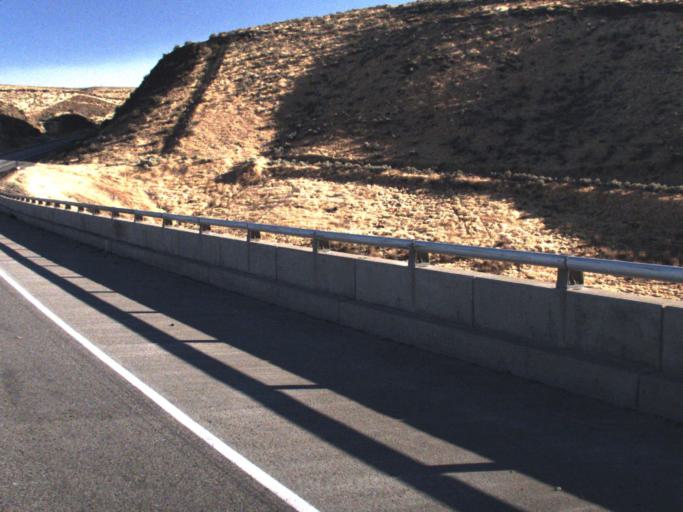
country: US
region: Washington
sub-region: Kittitas County
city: Kittitas
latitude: 46.7992
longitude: -120.3589
